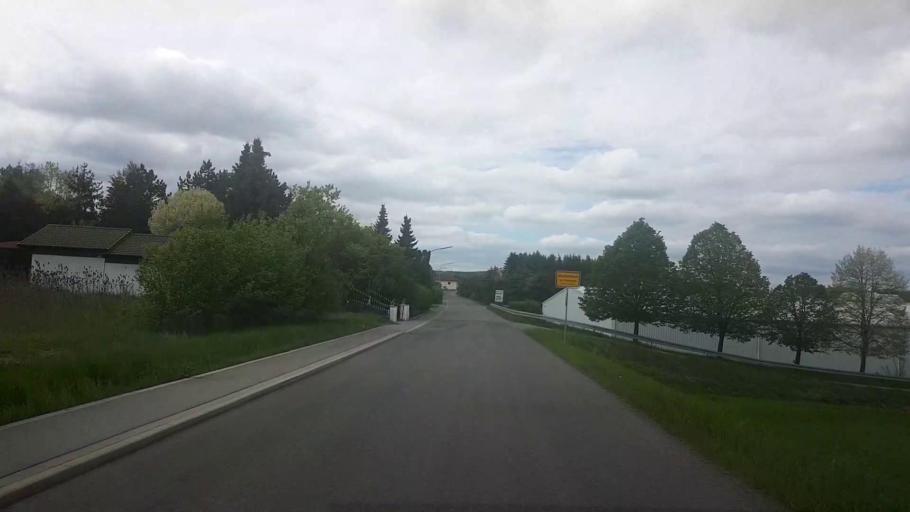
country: DE
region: Bavaria
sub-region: Upper Franconia
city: Untersiemau
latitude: 50.2023
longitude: 10.9807
